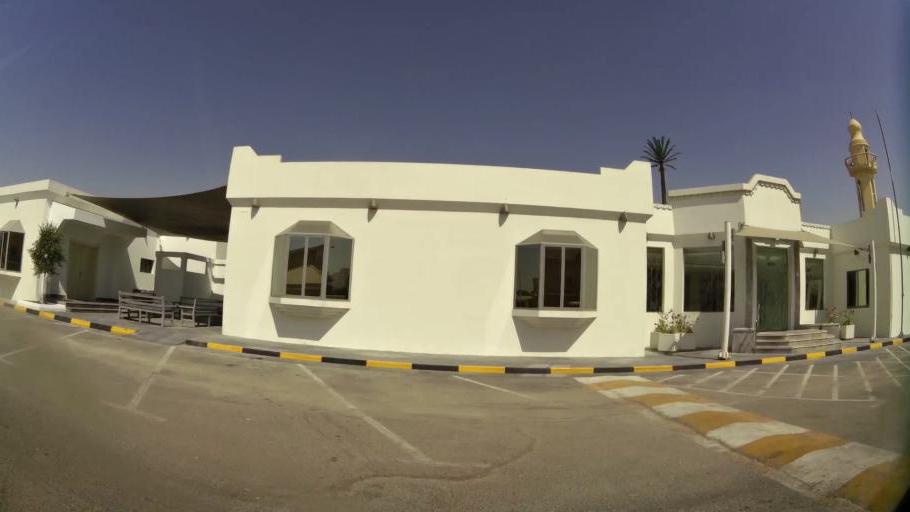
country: AE
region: Ajman
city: Ajman
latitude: 25.4040
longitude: 55.4775
